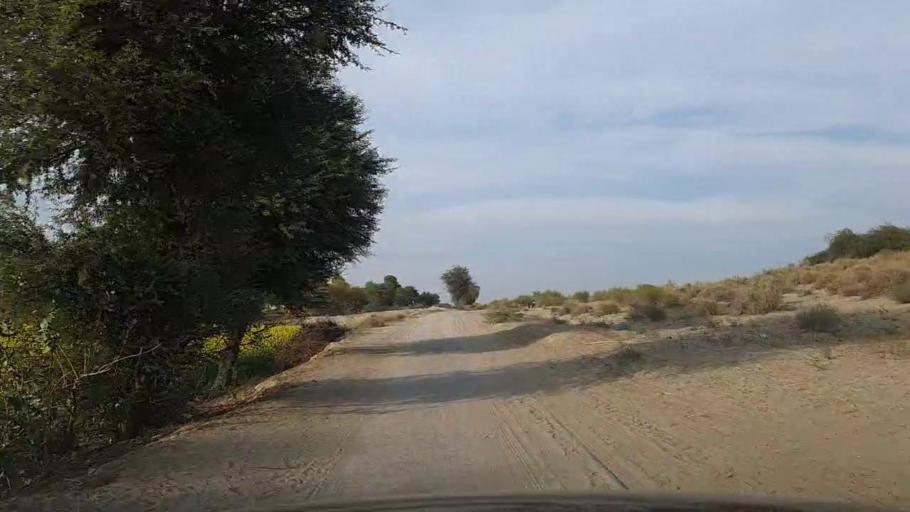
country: PK
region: Sindh
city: Jam Sahib
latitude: 26.4568
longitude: 68.5700
